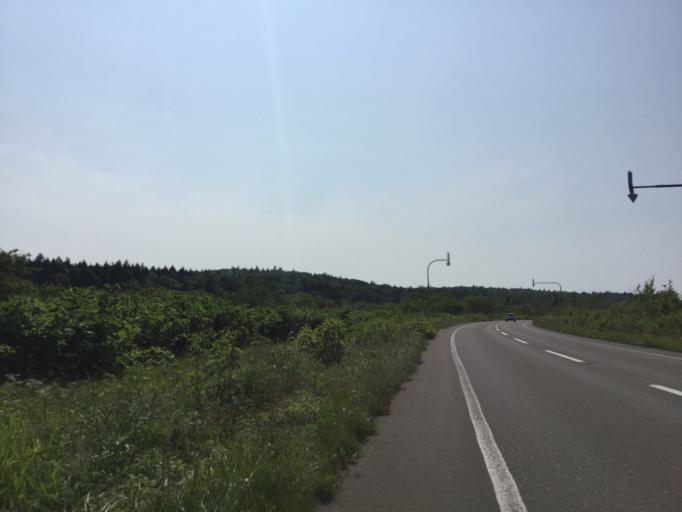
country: JP
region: Hokkaido
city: Makubetsu
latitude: 45.4045
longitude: 142.0269
